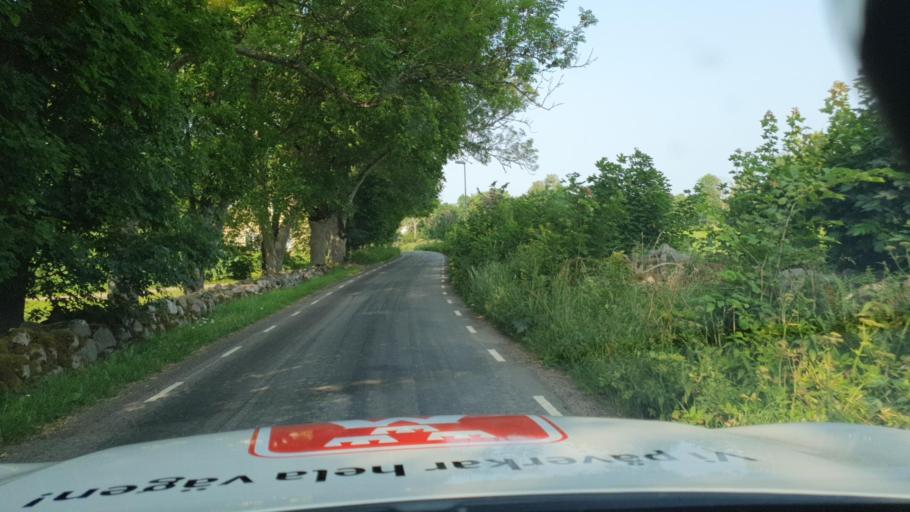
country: SE
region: Vaestra Goetaland
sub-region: Skovde Kommun
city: Stopen
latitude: 58.5017
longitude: 13.7750
